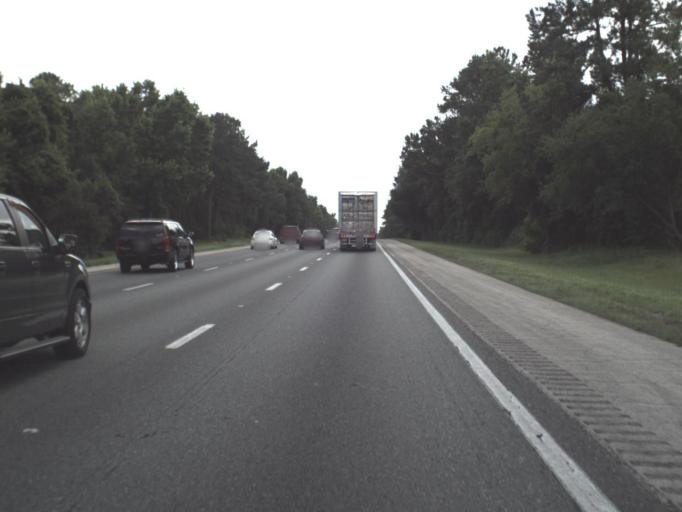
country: US
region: Florida
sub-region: Alachua County
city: Gainesville
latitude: 29.5510
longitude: -82.3394
